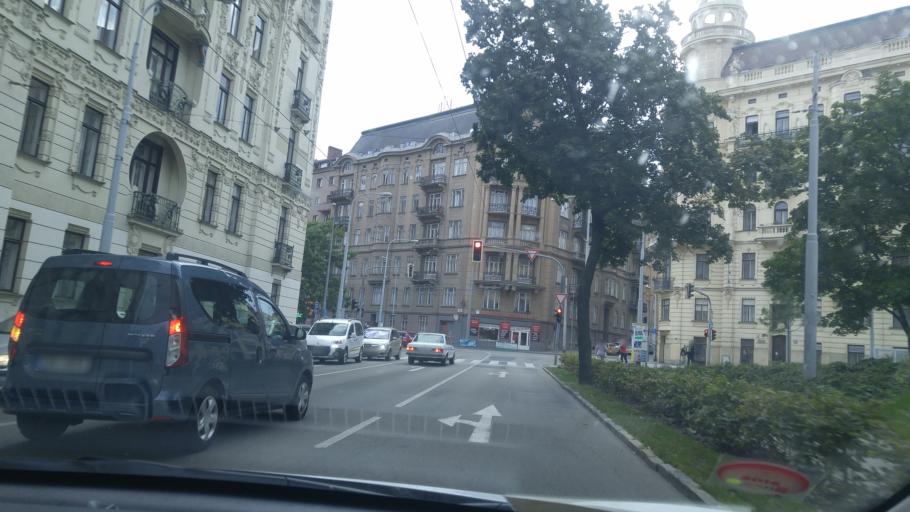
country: CZ
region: South Moravian
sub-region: Mesto Brno
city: Brno
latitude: 49.2046
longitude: 16.5948
